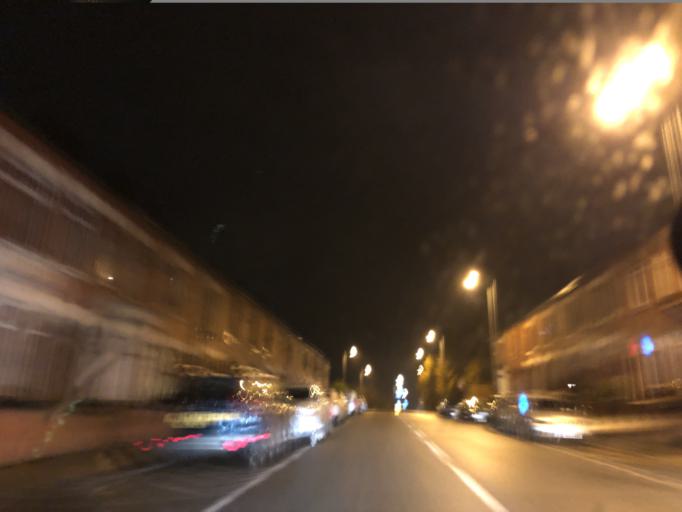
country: GB
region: England
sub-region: Borough of Oldham
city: Shaw
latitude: 53.5558
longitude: -2.0826
